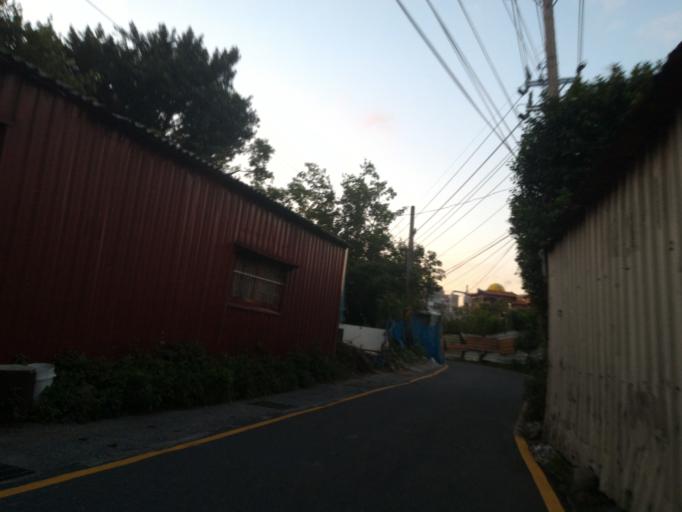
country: TW
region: Taipei
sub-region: Taipei
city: Banqiao
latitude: 24.9752
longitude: 121.4189
